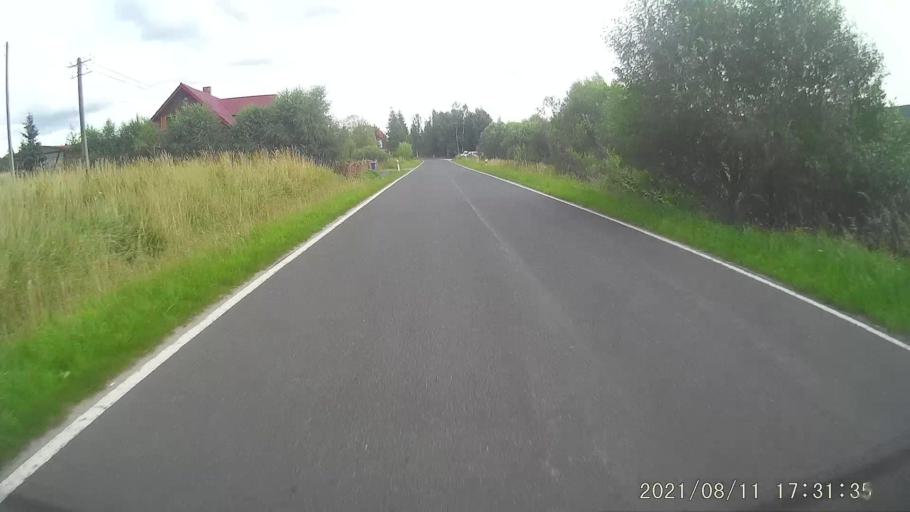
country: PL
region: Lower Silesian Voivodeship
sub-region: Powiat klodzki
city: Szczytna
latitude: 50.3019
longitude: 16.4549
